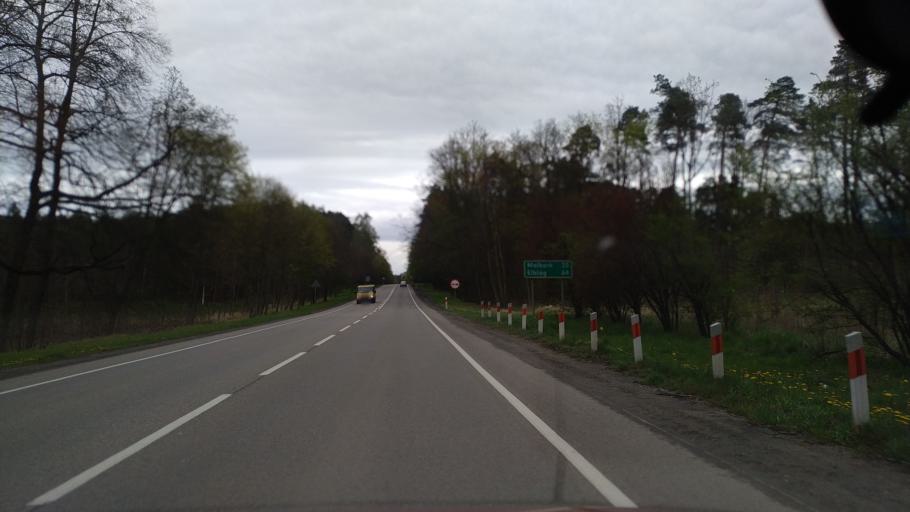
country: PL
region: Pomeranian Voivodeship
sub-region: Powiat starogardzki
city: Starogard Gdanski
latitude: 53.9790
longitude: 18.5651
